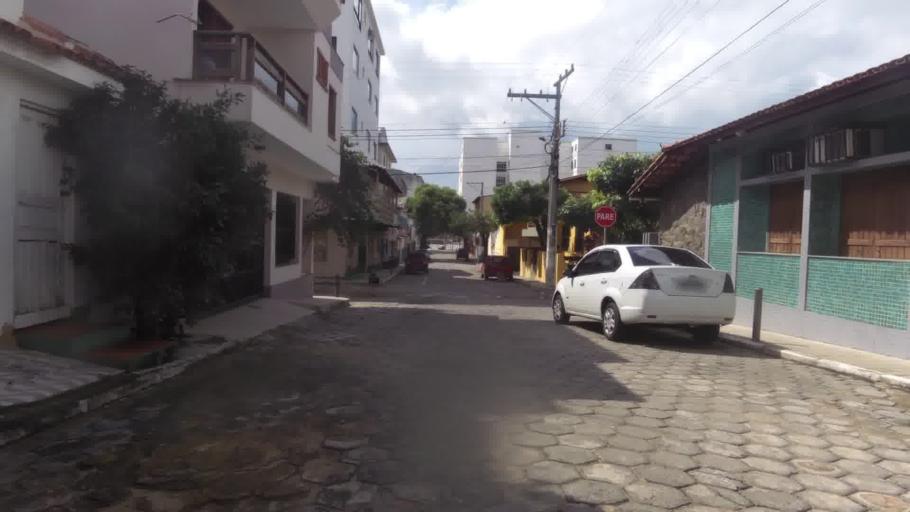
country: BR
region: Espirito Santo
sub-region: Piuma
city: Piuma
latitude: -20.8322
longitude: -40.6953
